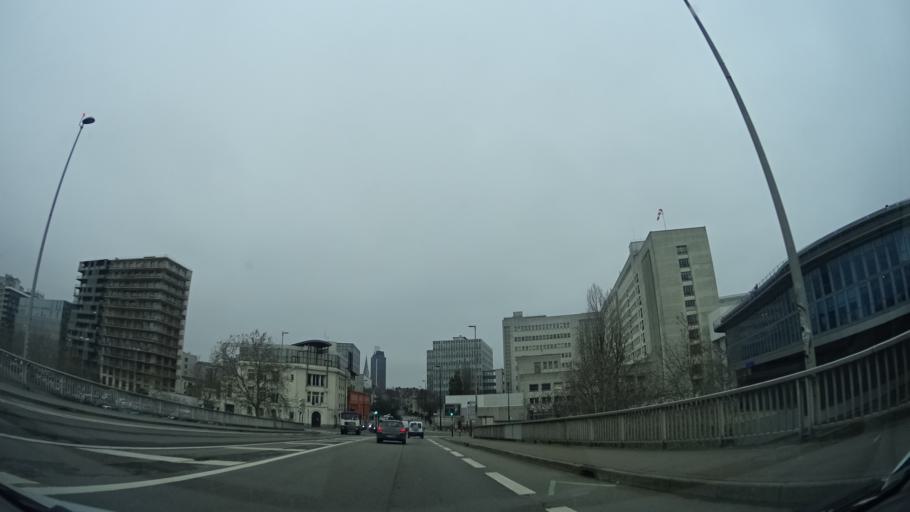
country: FR
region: Pays de la Loire
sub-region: Departement de la Loire-Atlantique
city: Nantes
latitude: 47.2085
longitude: -1.5554
